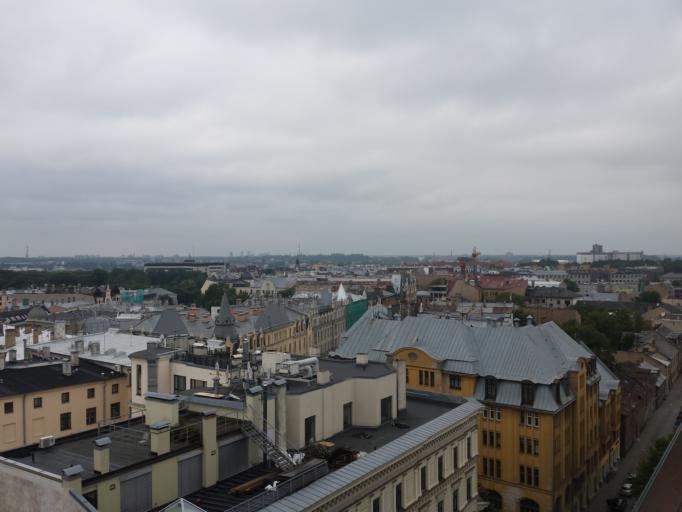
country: LV
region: Riga
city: Riga
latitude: 56.9584
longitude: 24.1132
